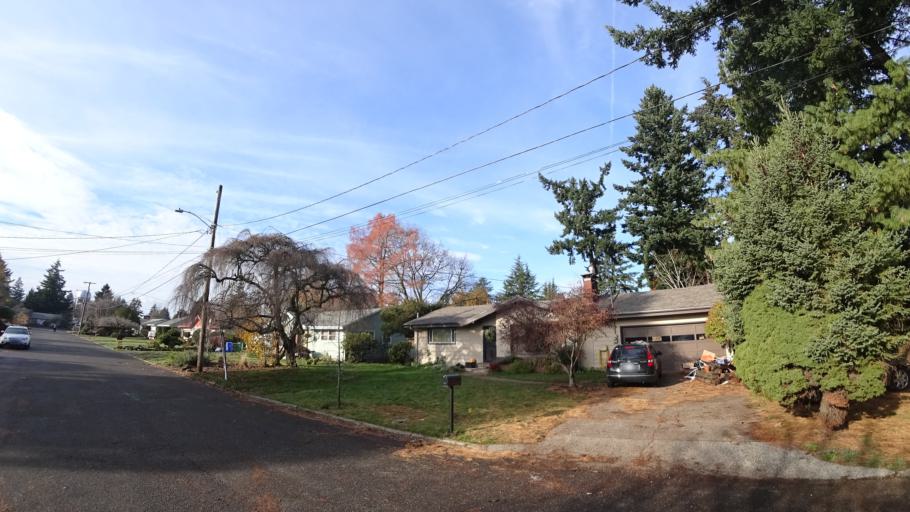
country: US
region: Oregon
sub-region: Multnomah County
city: Lents
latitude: 45.5210
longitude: -122.5275
